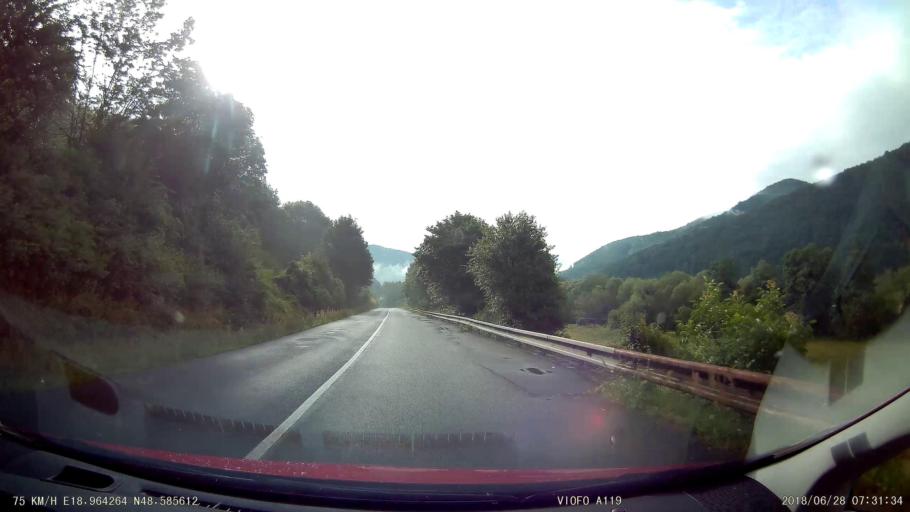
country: SK
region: Banskobystricky
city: Ziar nad Hronom
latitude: 48.5856
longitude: 18.9644
